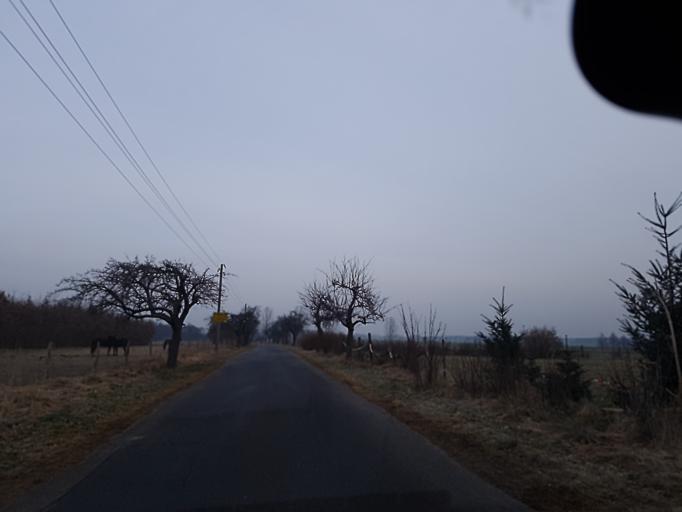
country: DE
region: Brandenburg
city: Ruckersdorf
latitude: 51.5663
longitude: 13.5454
